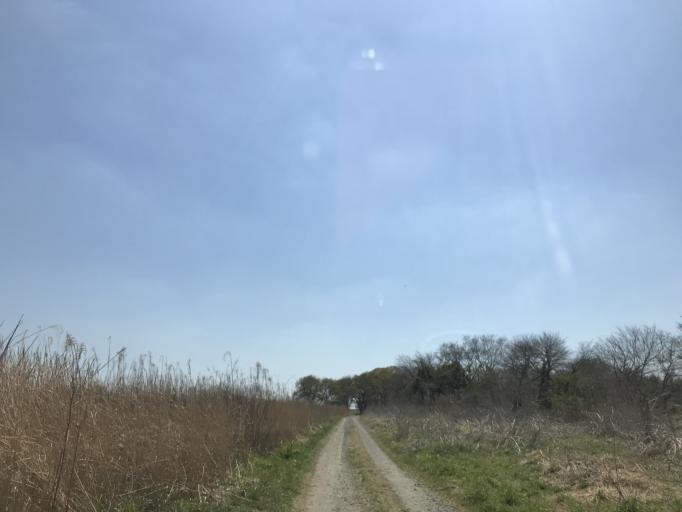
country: JP
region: Ibaraki
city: Moriya
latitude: 35.9324
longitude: 139.9742
